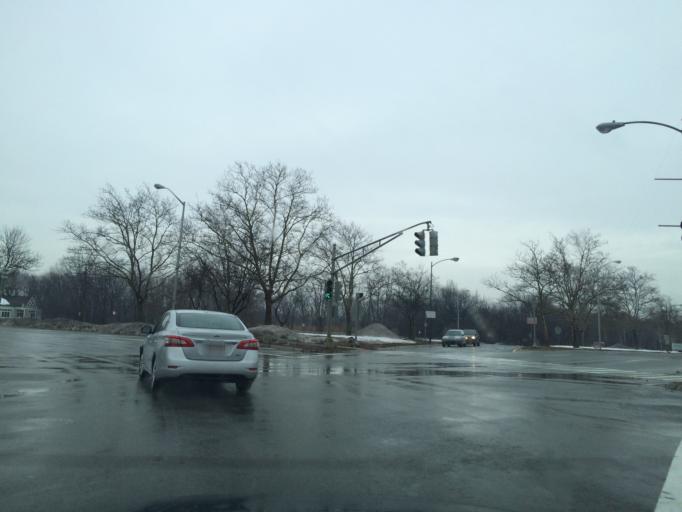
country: US
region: Massachusetts
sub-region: Middlesex County
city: Cambridge
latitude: 42.3713
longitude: -71.1348
